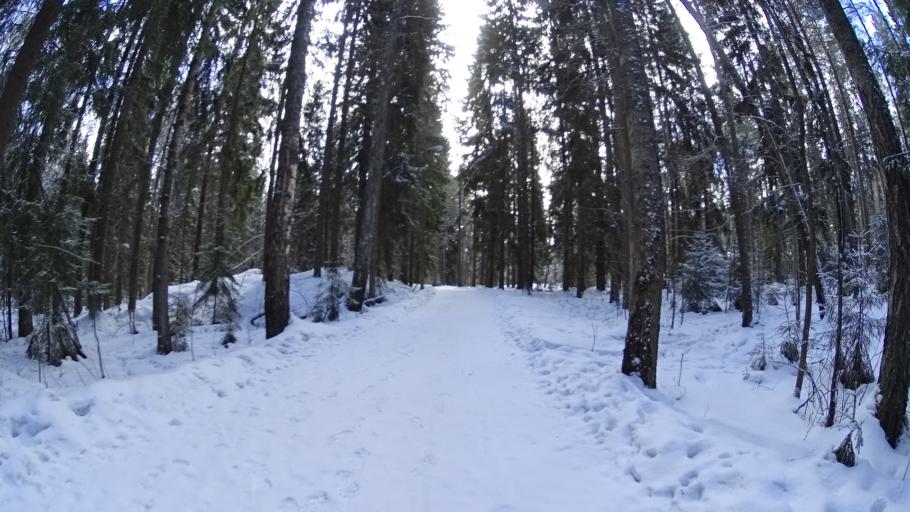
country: FI
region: Uusimaa
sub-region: Helsinki
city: Teekkarikylae
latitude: 60.2641
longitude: 24.8898
